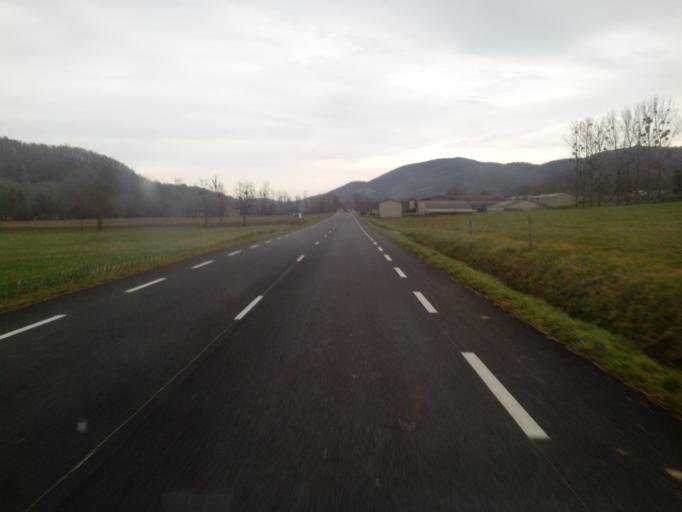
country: FR
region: Midi-Pyrenees
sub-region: Departement de l'Ariege
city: Foix
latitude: 43.0109
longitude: 1.4465
